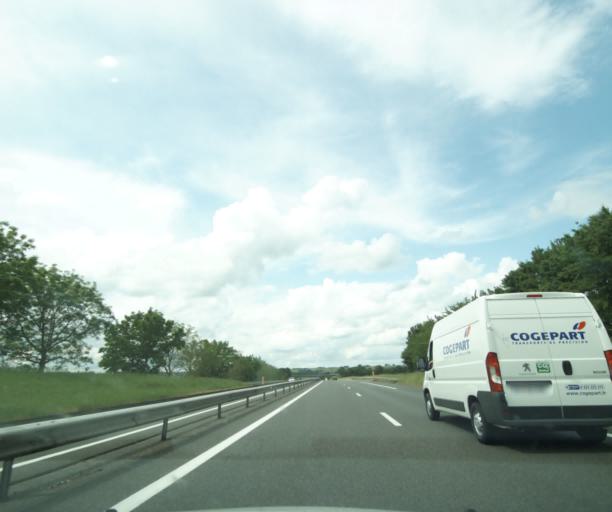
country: FR
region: Auvergne
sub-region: Departement de l'Allier
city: Bellenaves
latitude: 46.1960
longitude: 3.1061
